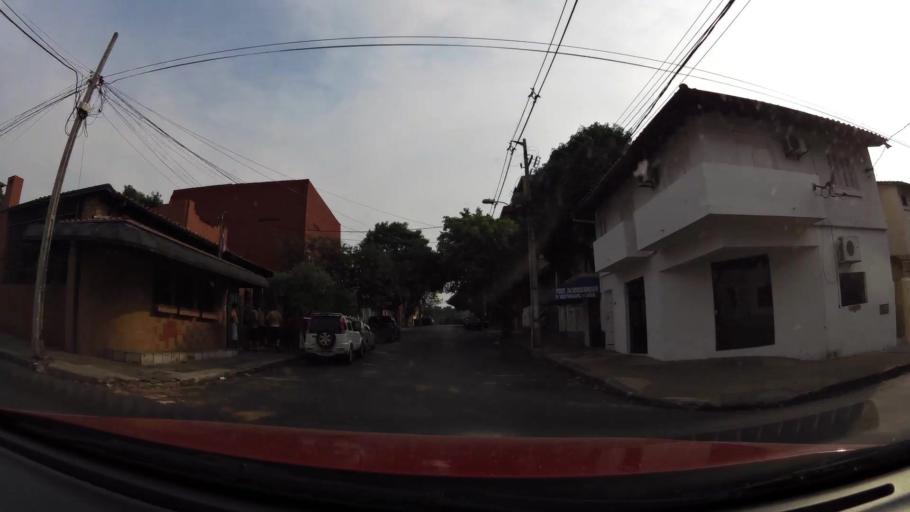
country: PY
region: Asuncion
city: Asuncion
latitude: -25.2958
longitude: -57.6198
